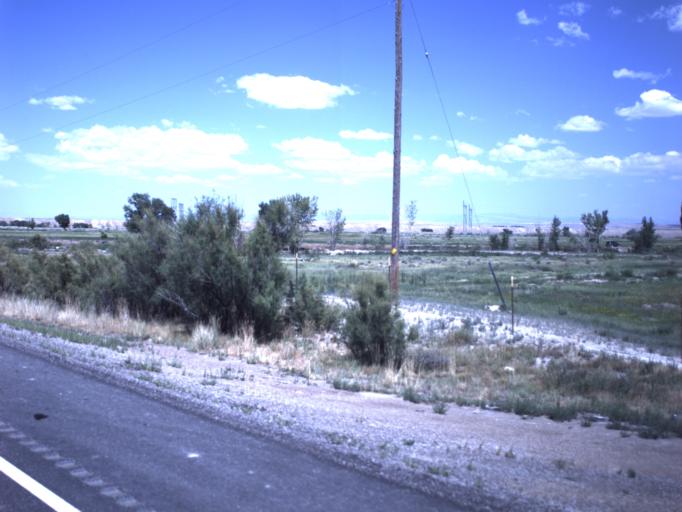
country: US
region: Utah
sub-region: Emery County
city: Castle Dale
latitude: 39.2530
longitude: -110.9855
